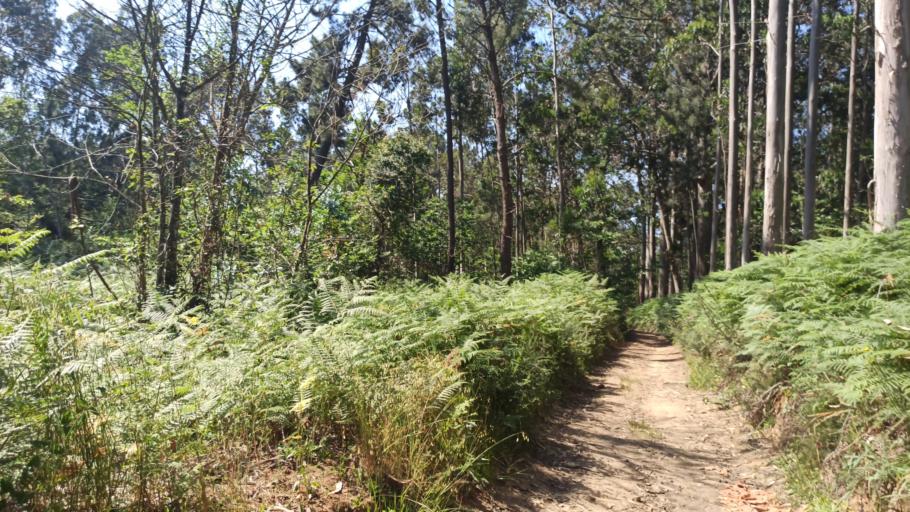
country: ES
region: Galicia
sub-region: Provincia da Coruna
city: Sada
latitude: 43.3802
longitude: -8.2706
